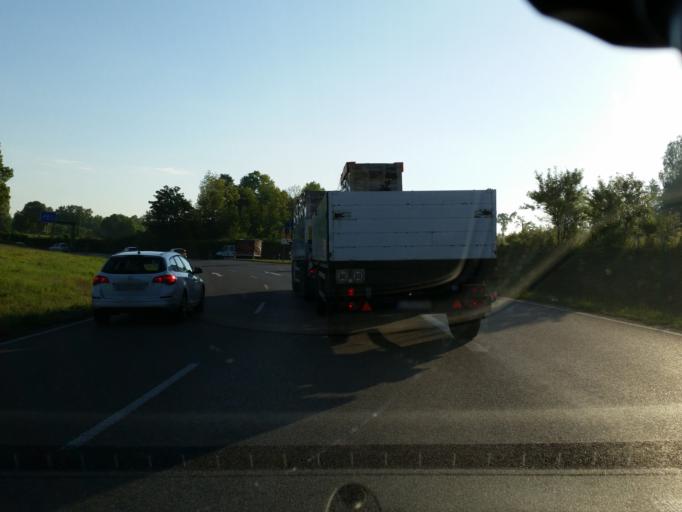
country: DE
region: Bavaria
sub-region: Upper Bavaria
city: Landsberg am Lech
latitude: 48.0468
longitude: 10.8393
